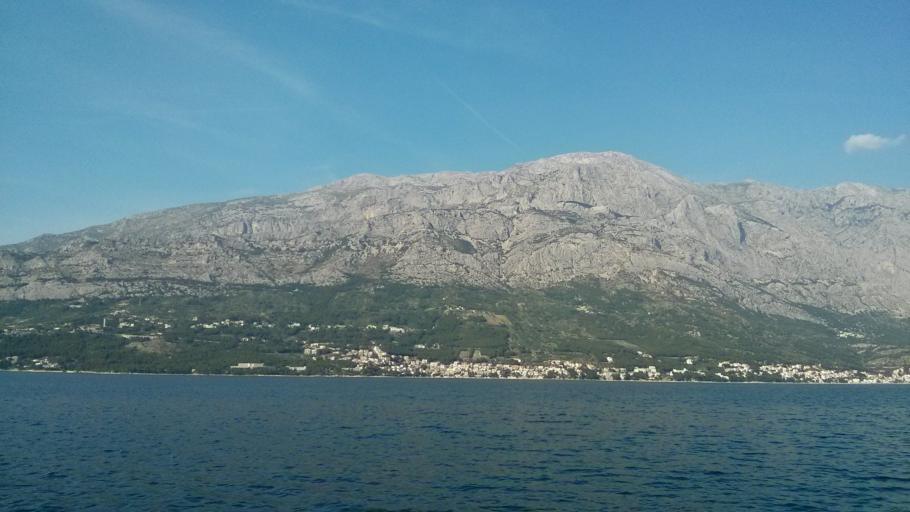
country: HR
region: Splitsko-Dalmatinska
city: Donja Brela
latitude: 43.3515
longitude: 16.9110
